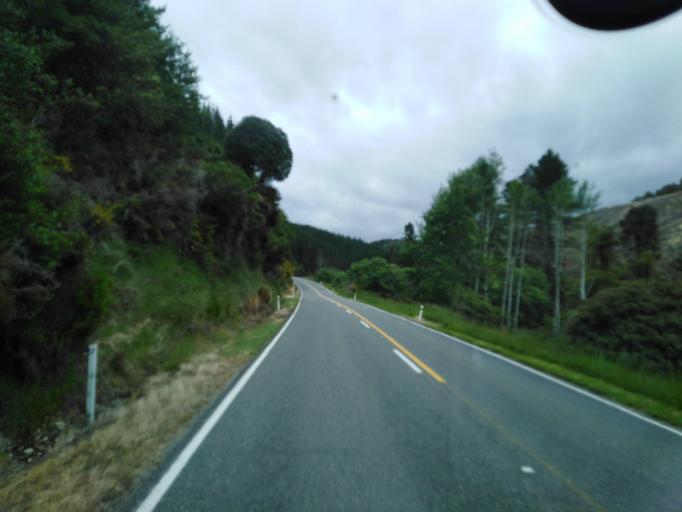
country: NZ
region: Tasman
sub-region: Tasman District
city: Wakefield
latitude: -41.6238
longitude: 172.7407
